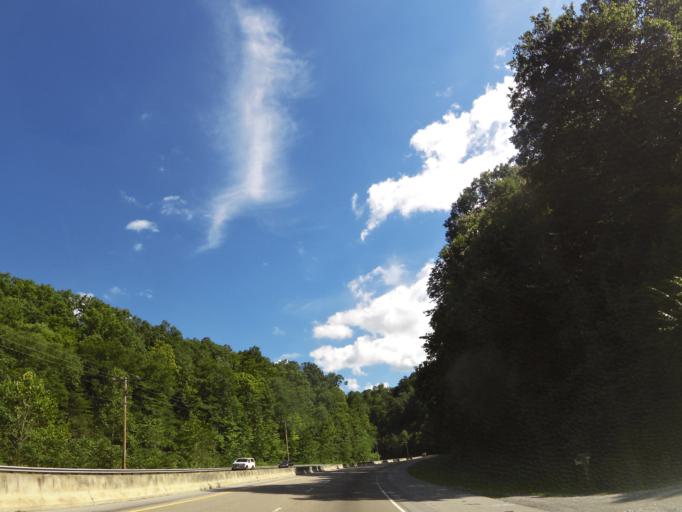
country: US
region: Tennessee
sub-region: Grainger County
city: Rutledge
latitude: 36.3714
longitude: -83.4387
